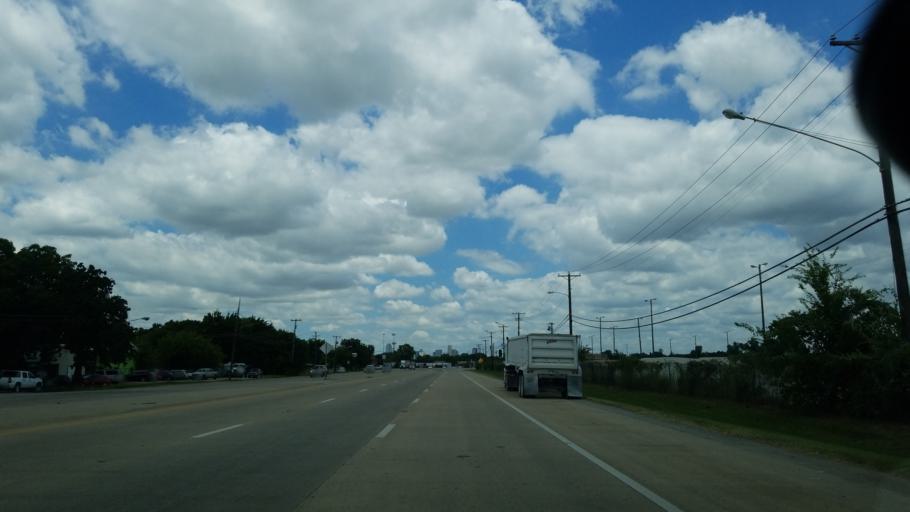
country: US
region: Texas
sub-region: Dallas County
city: Hutchins
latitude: 32.7169
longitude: -96.7560
